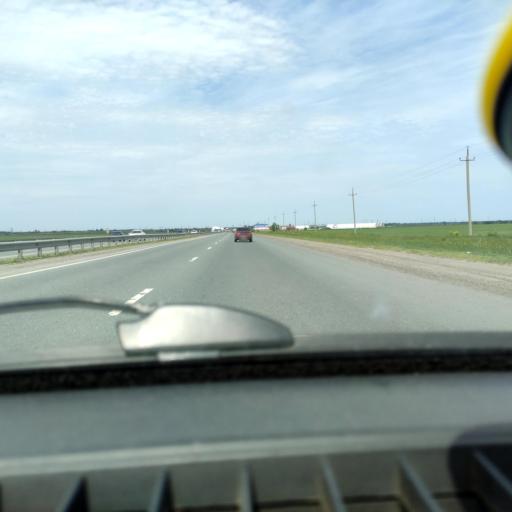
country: RU
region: Samara
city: Zhigulevsk
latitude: 53.5492
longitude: 49.5097
